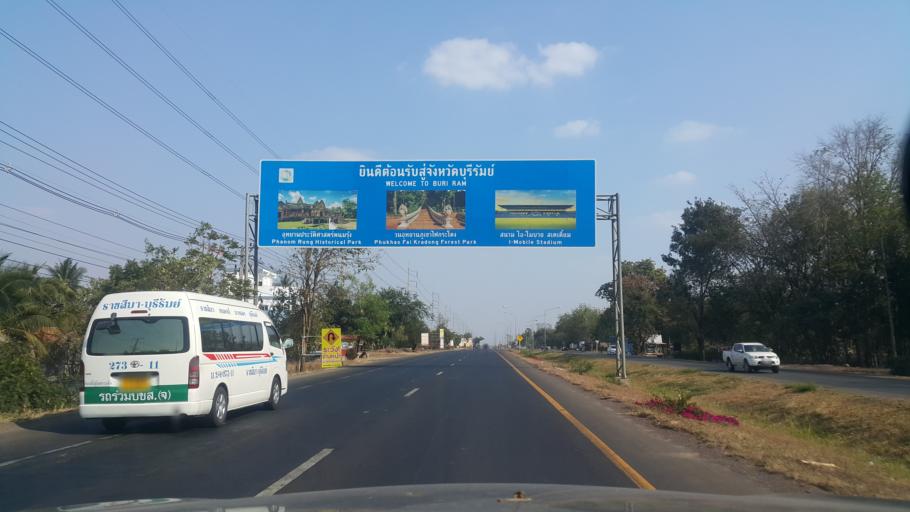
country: TH
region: Buriram
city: Nong Ki
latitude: 14.7078
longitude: 102.4688
